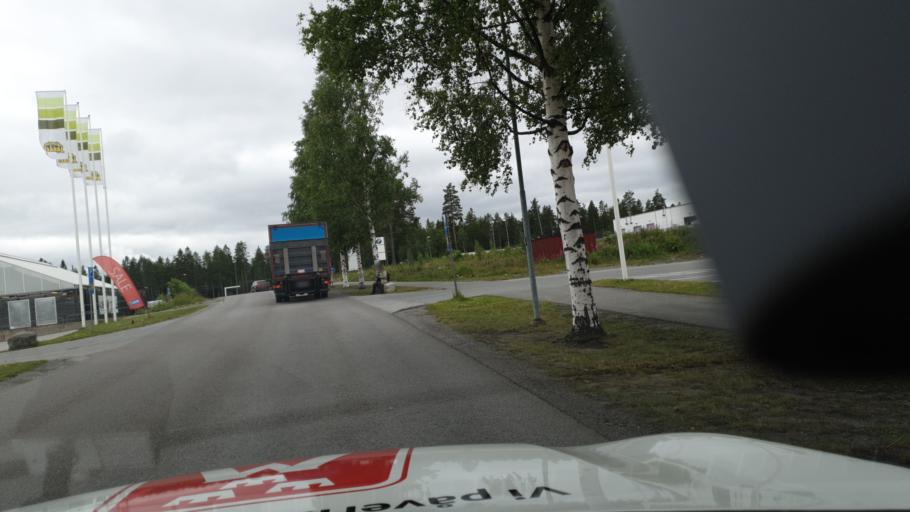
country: SE
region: Vaesterbotten
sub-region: Skelleftea Kommun
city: Skelleftea
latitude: 64.7666
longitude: 21.0206
